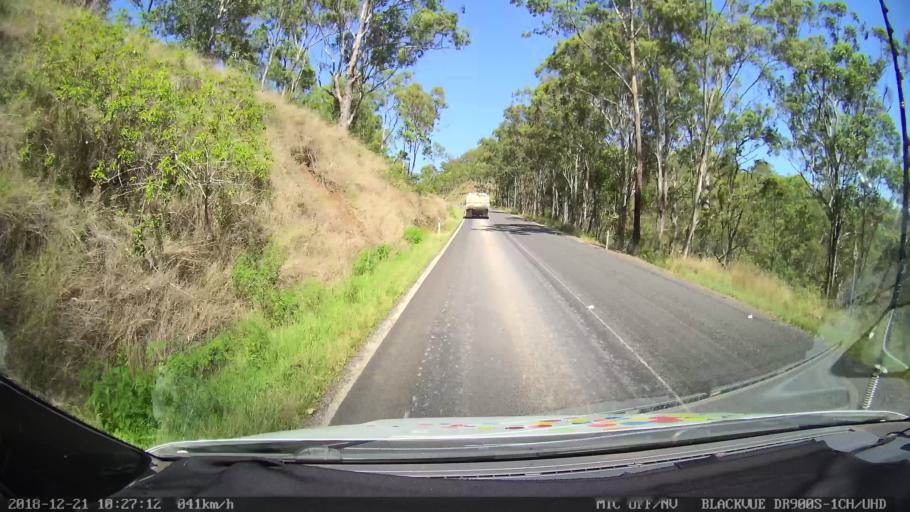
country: AU
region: New South Wales
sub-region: Clarence Valley
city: South Grafton
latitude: -29.6305
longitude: 152.7425
